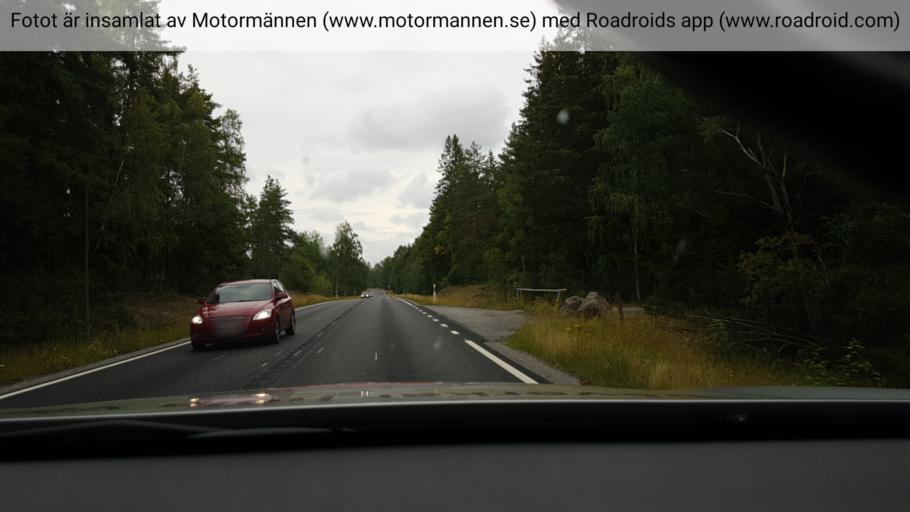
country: SE
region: Soedermanland
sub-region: Strangnas Kommun
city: Strangnas
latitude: 59.3171
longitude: 17.0035
